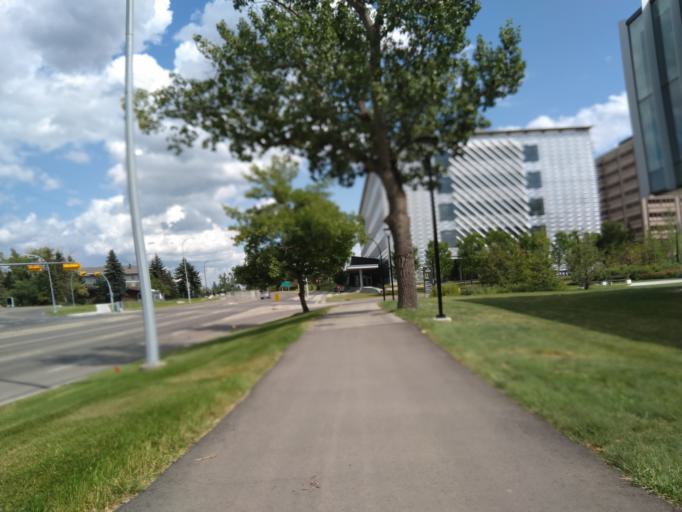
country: CA
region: Alberta
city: Calgary
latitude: 51.0813
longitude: -114.1316
